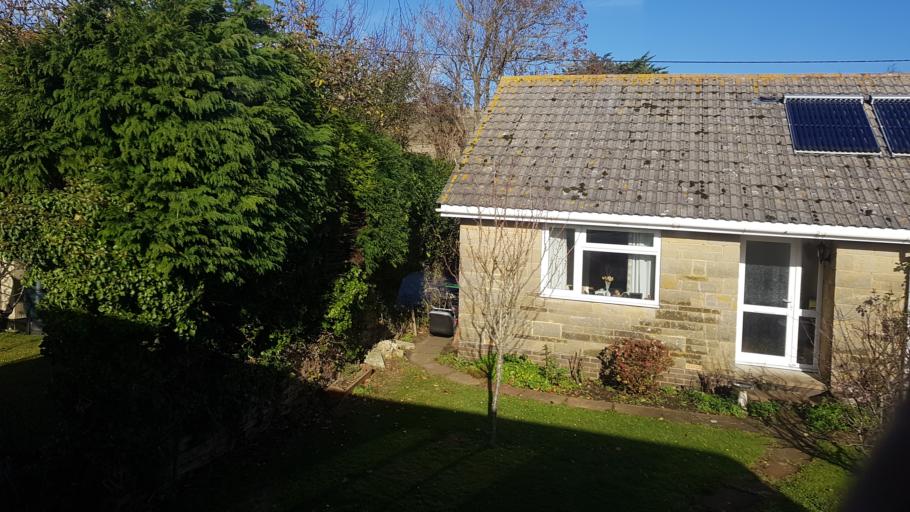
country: GB
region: England
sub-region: Isle of Wight
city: Shalfleet
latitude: 50.6422
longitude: -1.3745
